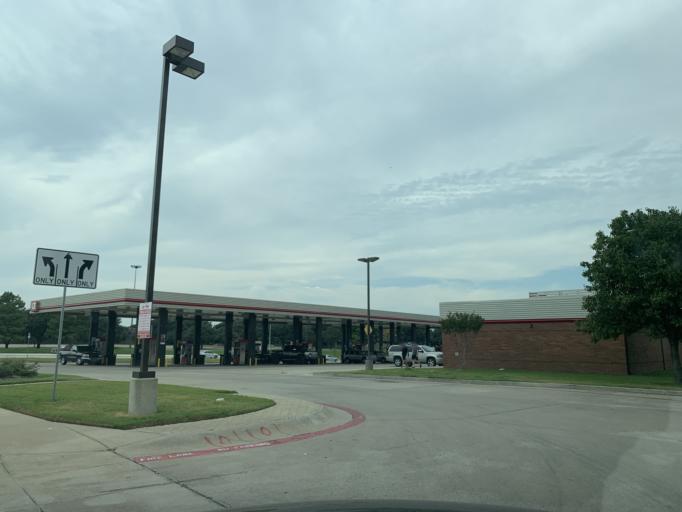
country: US
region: Texas
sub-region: Tarrant County
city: Watauga
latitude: 32.8439
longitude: -97.2895
